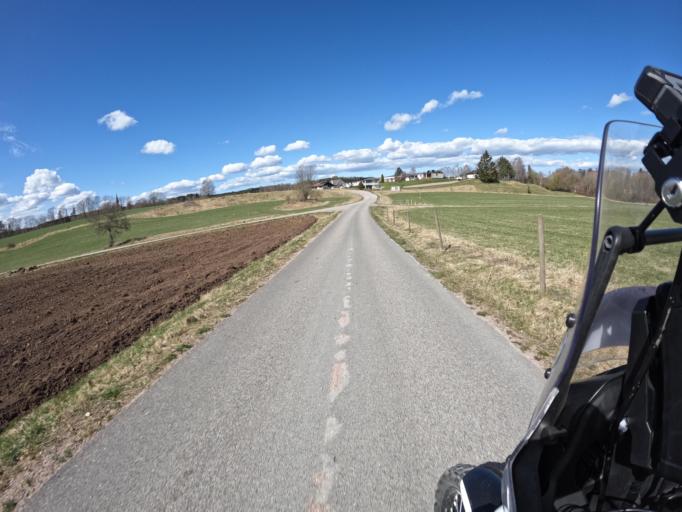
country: SE
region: Vaestra Goetaland
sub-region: Ulricehamns Kommun
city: Ulricehamn
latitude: 57.9276
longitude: 13.5001
